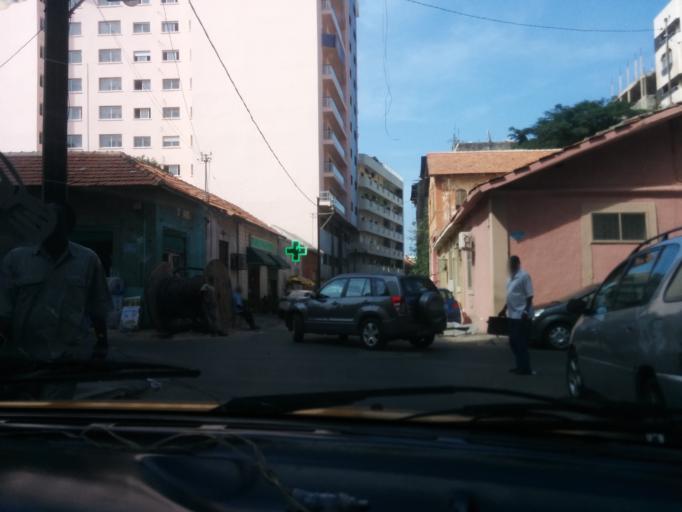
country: SN
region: Dakar
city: Dakar
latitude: 14.6716
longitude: -17.4340
